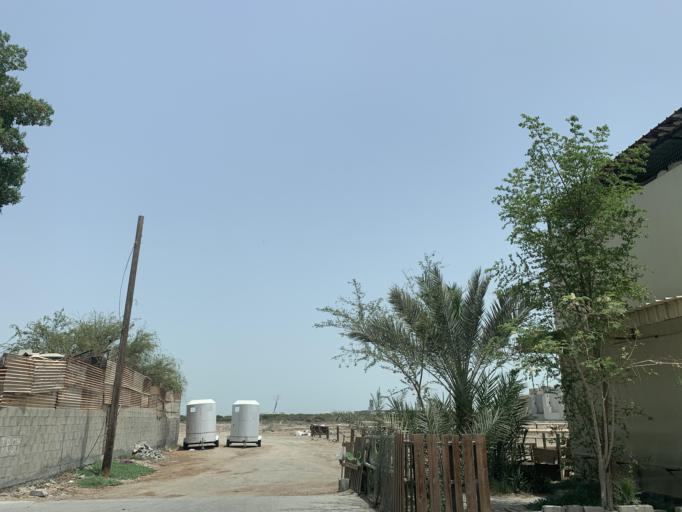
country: BH
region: Northern
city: Sitrah
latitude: 26.1506
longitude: 50.5874
